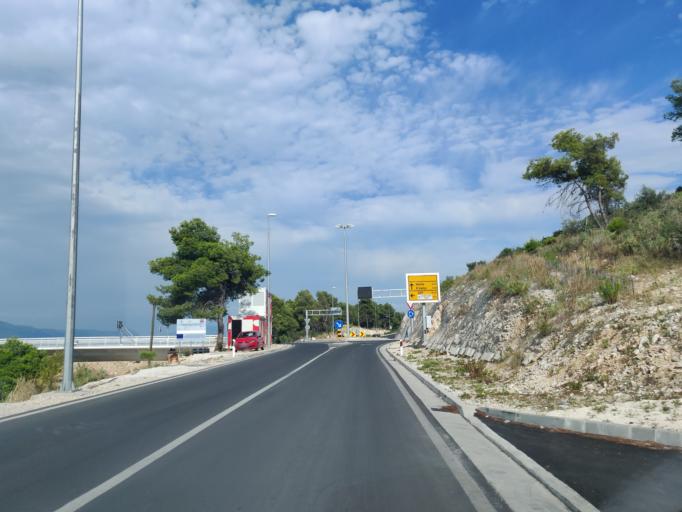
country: HR
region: Splitsko-Dalmatinska
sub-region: Grad Trogir
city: Trogir
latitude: 43.5164
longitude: 16.2640
